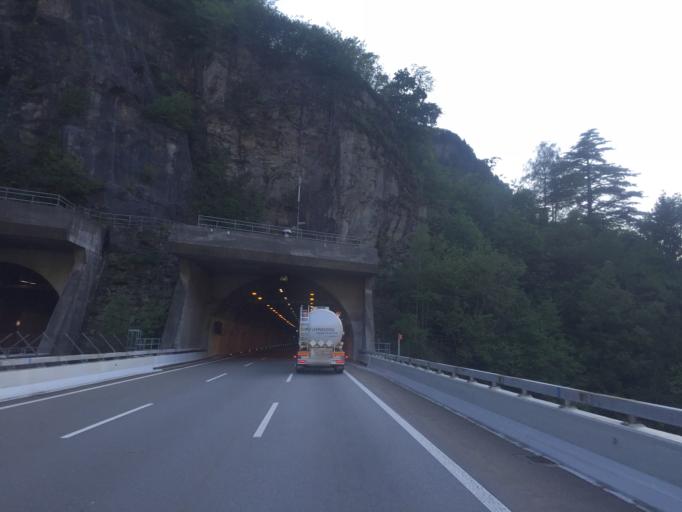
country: CH
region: Ticino
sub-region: Leventina District
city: Faido
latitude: 46.4746
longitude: 8.8007
